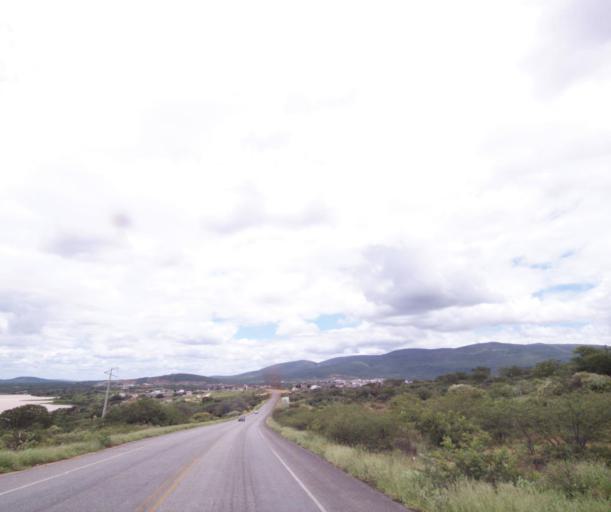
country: BR
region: Bahia
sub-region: Brumado
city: Brumado
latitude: -14.2176
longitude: -41.6581
